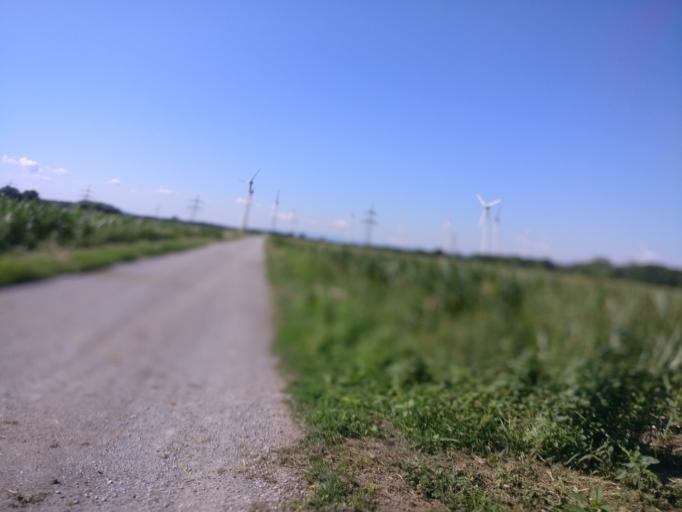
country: AT
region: Lower Austria
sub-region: Politischer Bezirk Baden
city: Ebreichsdorf
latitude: 47.9475
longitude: 16.3851
